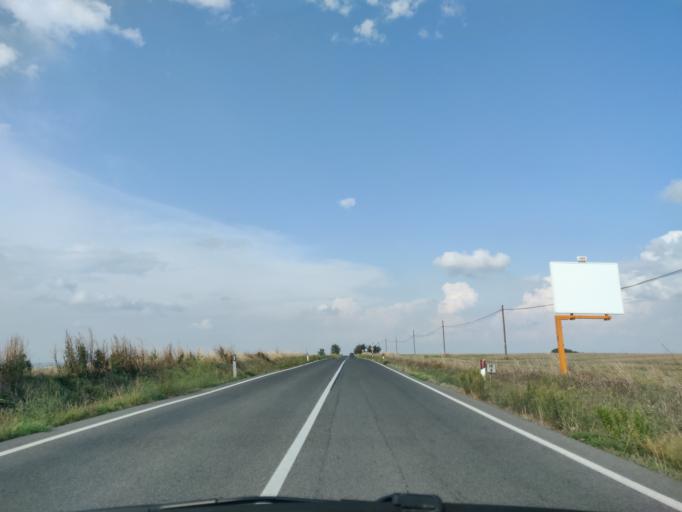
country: IT
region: Latium
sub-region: Provincia di Viterbo
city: Tarquinia
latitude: 42.2420
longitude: 11.8066
